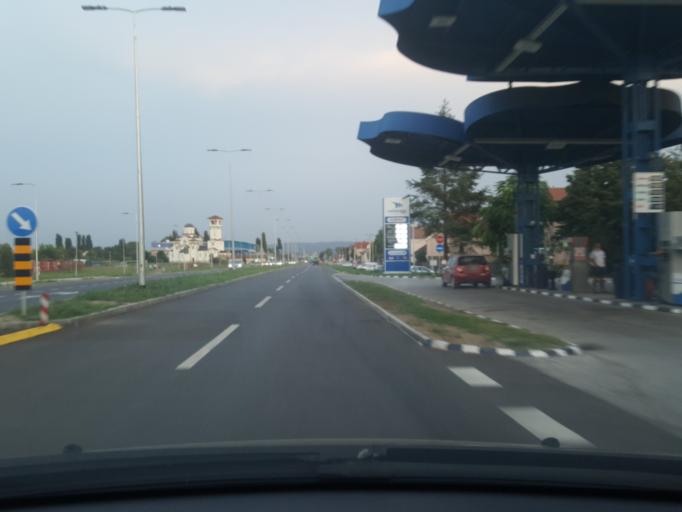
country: RS
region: Autonomna Pokrajina Vojvodina
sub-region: Juznobacki Okrug
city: Novi Sad
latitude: 45.2952
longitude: 19.8227
